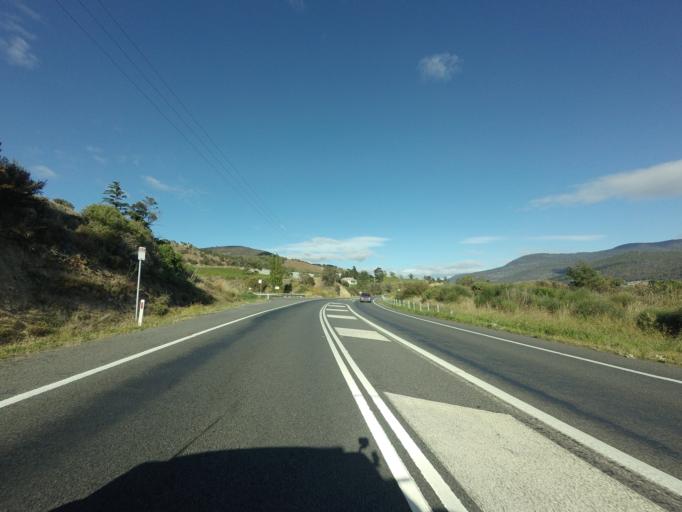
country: AU
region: Tasmania
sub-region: Brighton
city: Bridgewater
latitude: -42.7430
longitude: 147.1930
